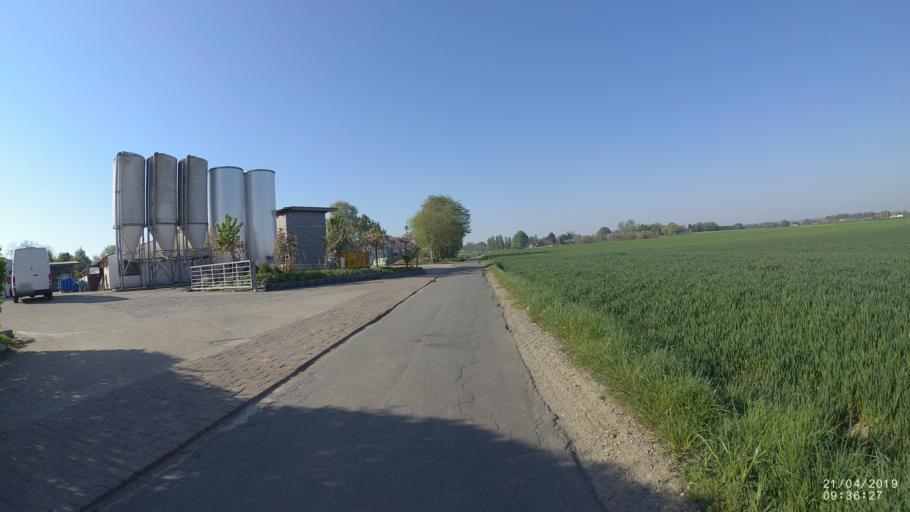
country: BE
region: Flanders
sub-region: Provincie Vlaams-Brabant
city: Lubbeek
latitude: 50.9236
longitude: 4.8351
